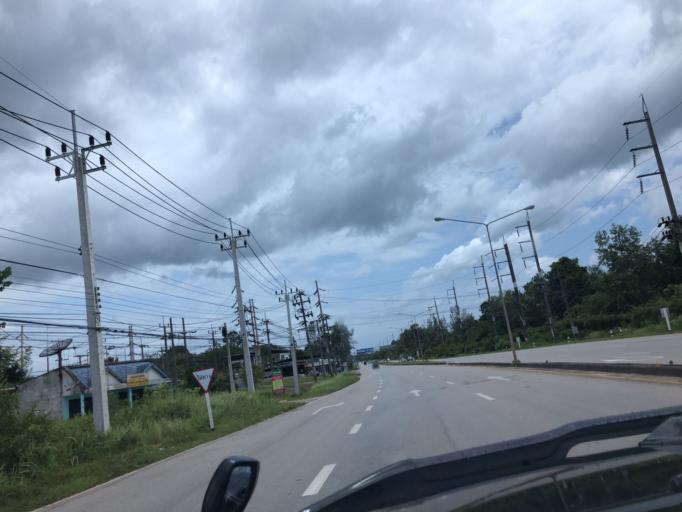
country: TH
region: Krabi
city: Khlong Thom
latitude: 7.9684
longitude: 99.1408
